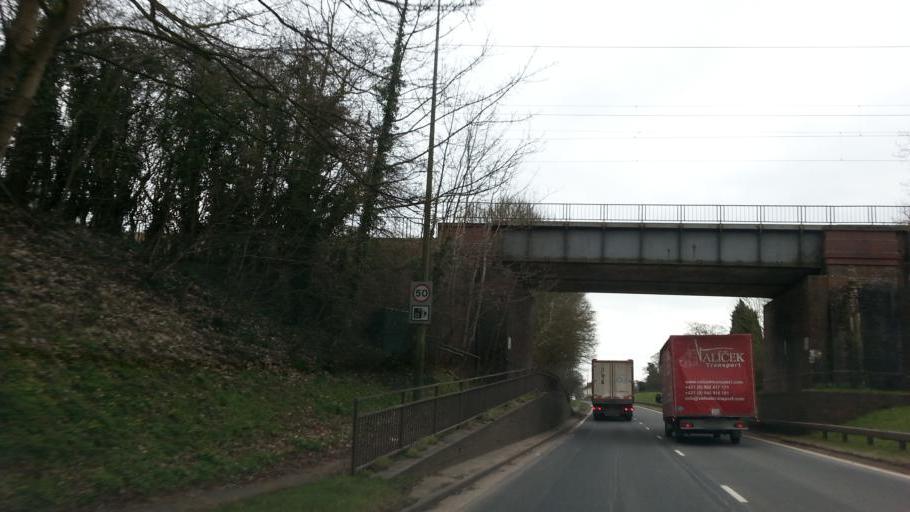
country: GB
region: England
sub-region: Staffordshire
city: Stone
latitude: 52.9021
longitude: -2.1588
